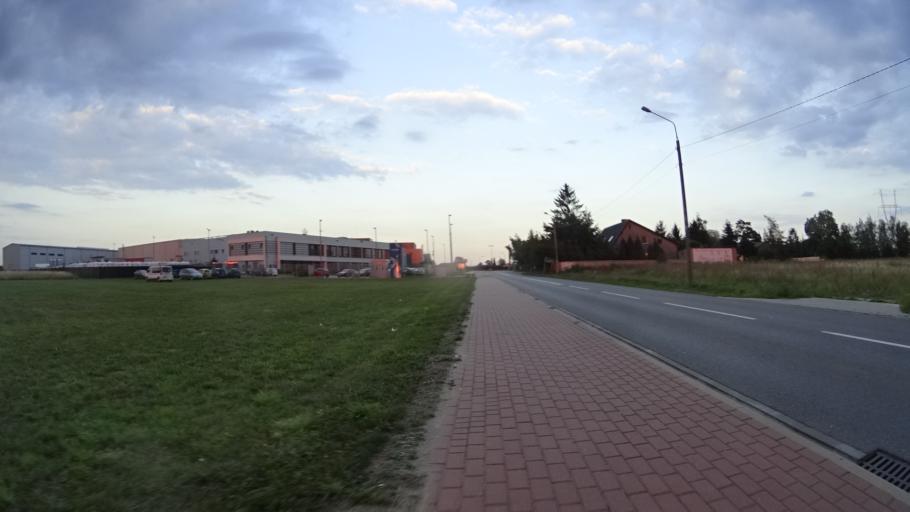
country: PL
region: Masovian Voivodeship
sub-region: Powiat warszawski zachodni
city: Babice
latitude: 52.2305
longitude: 20.8315
